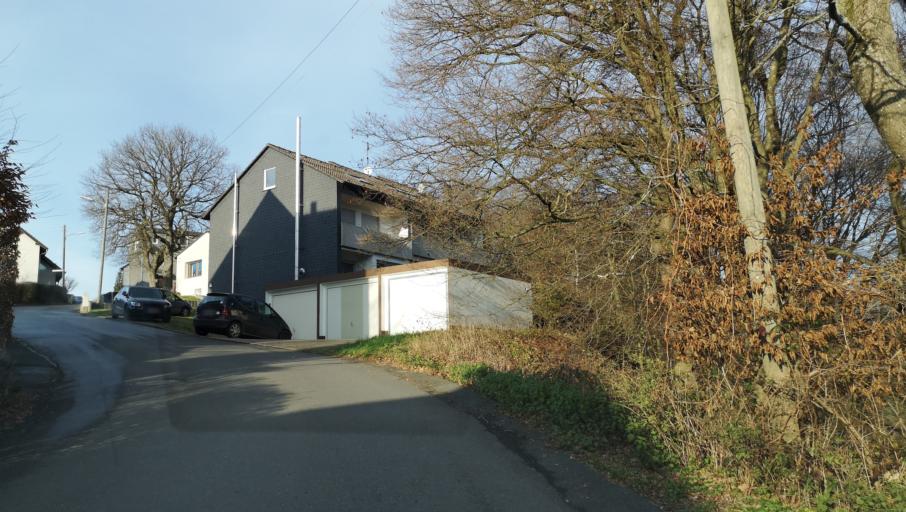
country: DE
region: North Rhine-Westphalia
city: Radevormwald
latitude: 51.2240
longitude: 7.3154
